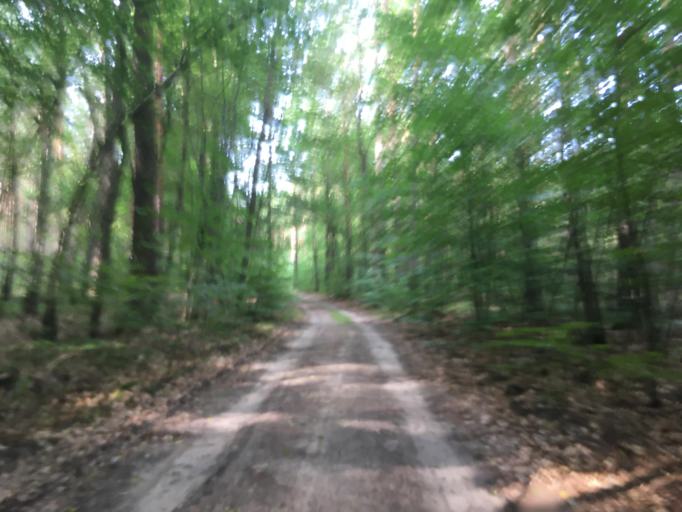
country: DE
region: Brandenburg
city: Eberswalde
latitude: 52.7904
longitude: 13.8231
